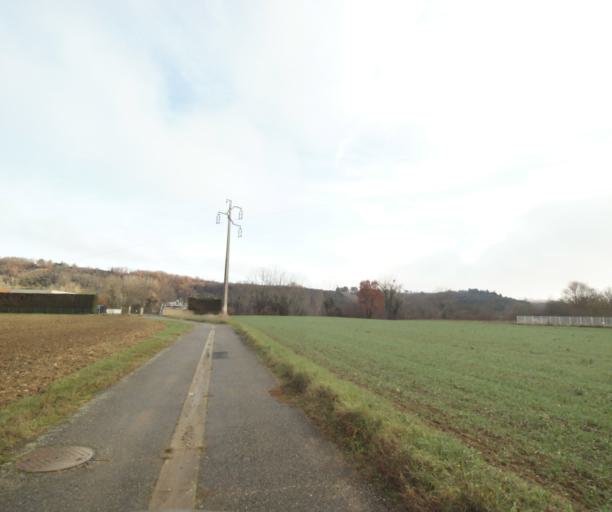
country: FR
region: Midi-Pyrenees
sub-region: Departement de la Haute-Garonne
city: Villemur-sur-Tarn
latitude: 43.8716
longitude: 1.4952
